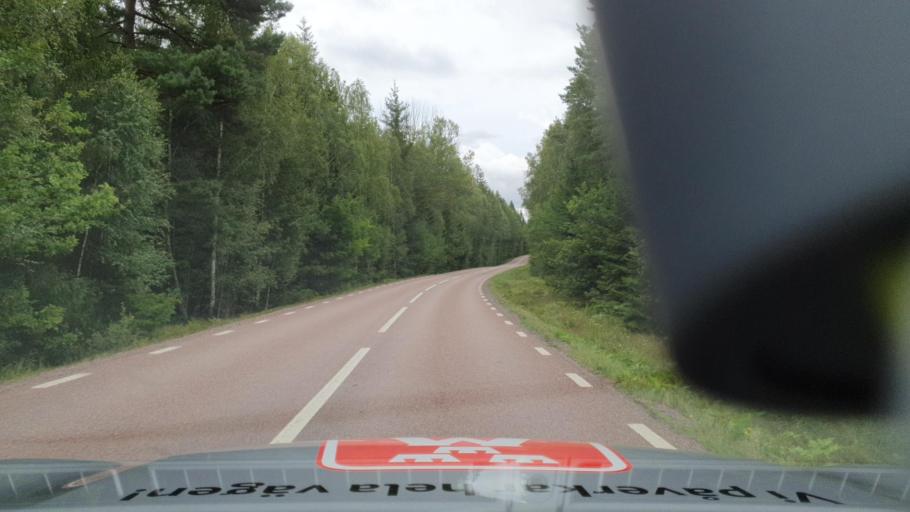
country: SE
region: Kalmar
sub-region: Monsteras Kommun
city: Blomstermala
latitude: 56.9375
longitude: 16.1882
